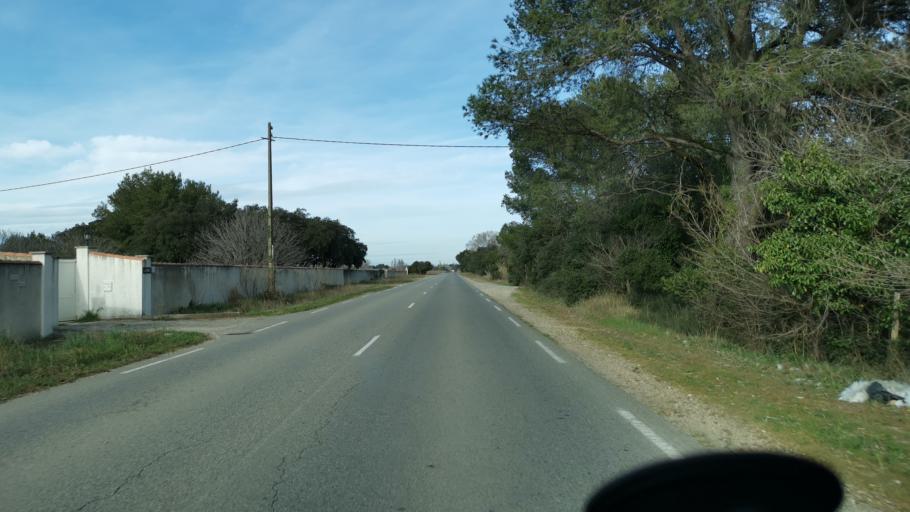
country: FR
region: Provence-Alpes-Cote d'Azur
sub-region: Departement des Bouches-du-Rhone
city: Saint-Martin-de-Crau
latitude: 43.5695
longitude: 4.7442
